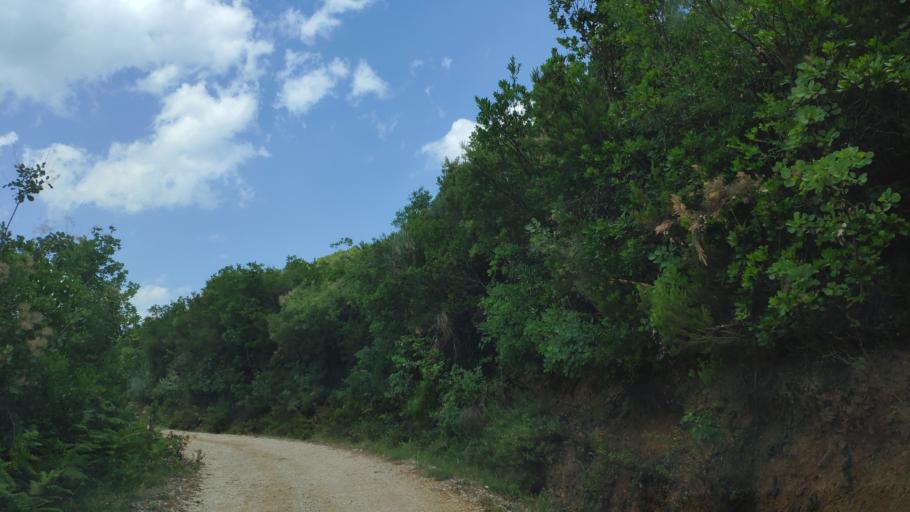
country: GR
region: Epirus
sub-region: Nomos Artas
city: Agios Dimitrios
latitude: 39.3174
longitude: 21.0108
